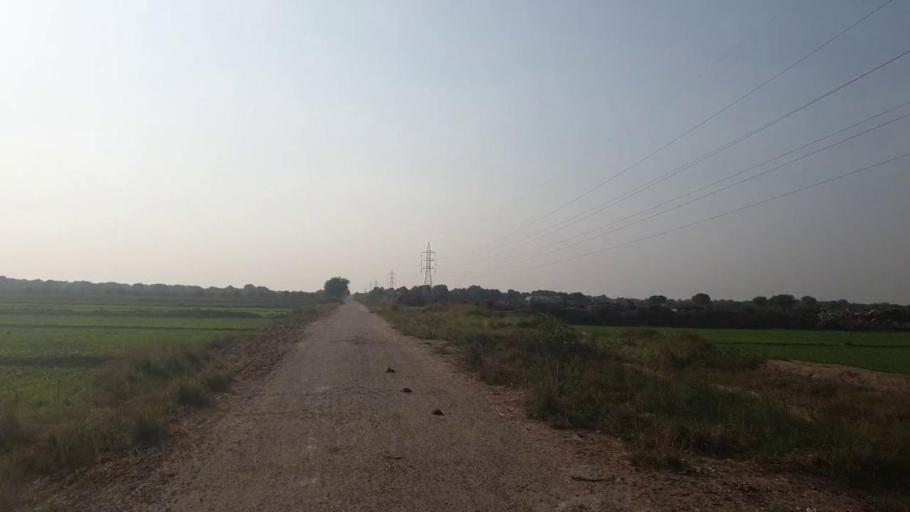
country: PK
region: Sindh
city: Tando Jam
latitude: 25.4267
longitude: 68.4766
